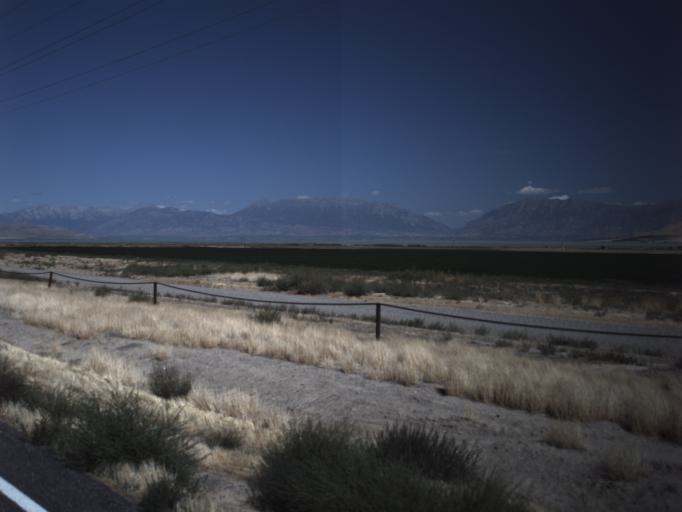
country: US
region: Utah
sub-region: Utah County
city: Genola
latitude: 40.0571
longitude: -111.9584
